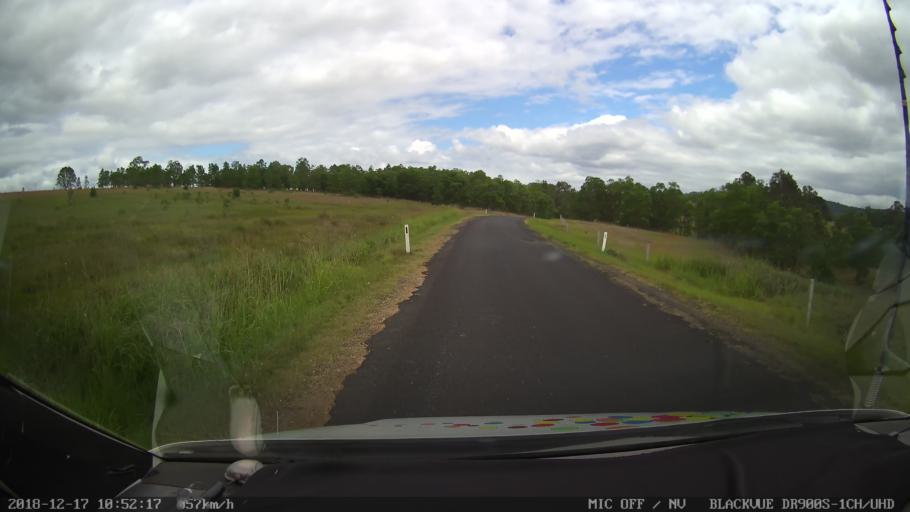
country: AU
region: New South Wales
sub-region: Tenterfield Municipality
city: Carrolls Creek
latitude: -28.8465
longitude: 152.5643
